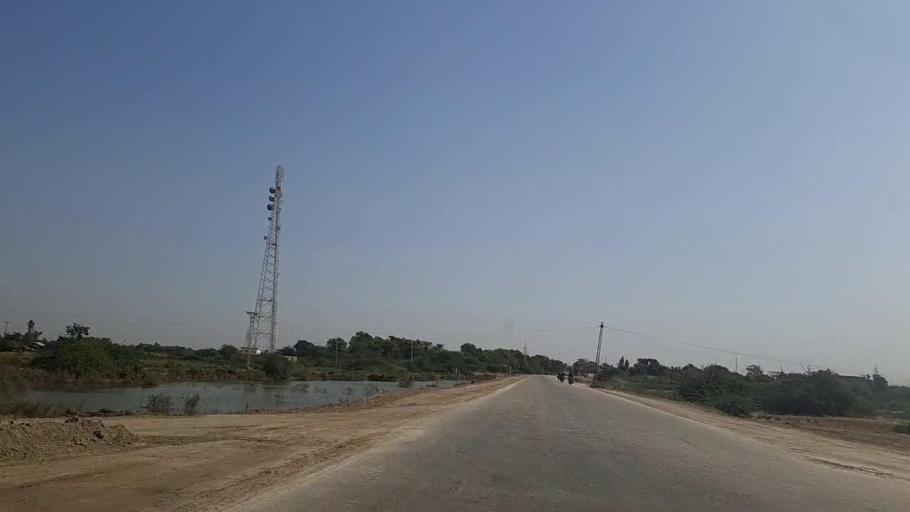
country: PK
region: Sindh
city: Mirpur Batoro
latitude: 24.7384
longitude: 68.2527
